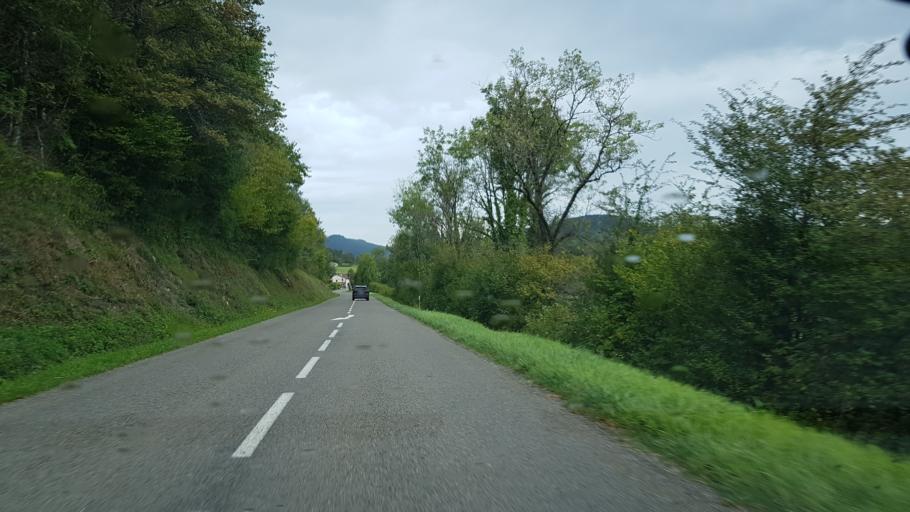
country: FR
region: Rhone-Alpes
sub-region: Departement de l'Ain
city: Cuisiat
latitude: 46.3322
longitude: 5.4372
